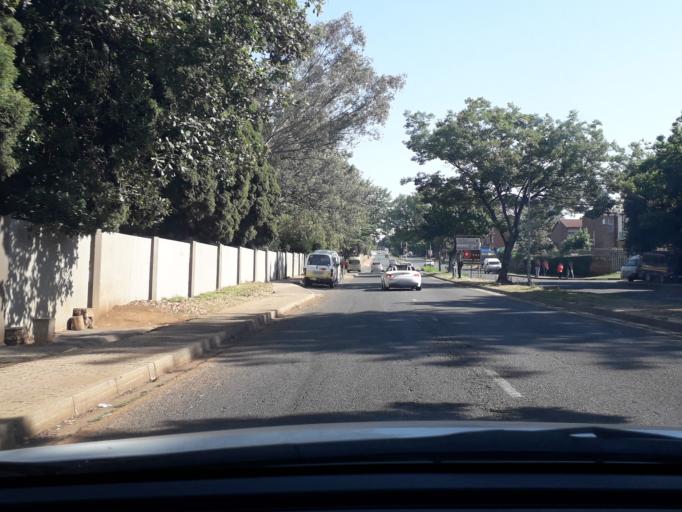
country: ZA
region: Gauteng
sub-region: City of Johannesburg Metropolitan Municipality
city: Johannesburg
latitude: -26.1224
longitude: 27.9738
